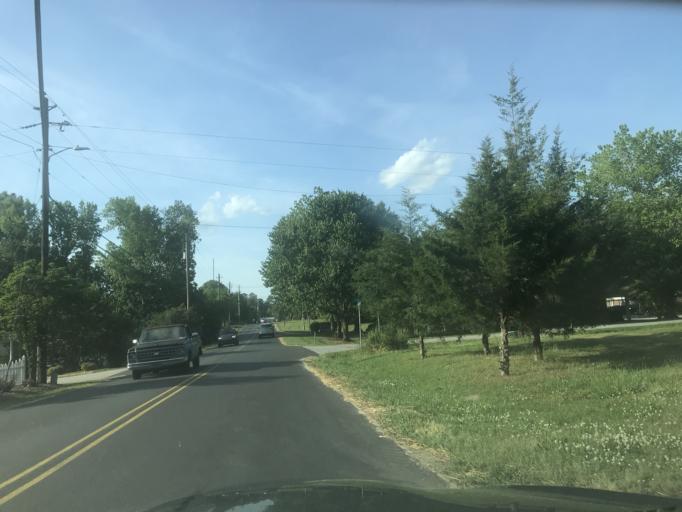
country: US
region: North Carolina
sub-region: Wake County
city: Wendell
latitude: 35.7780
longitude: -78.3664
